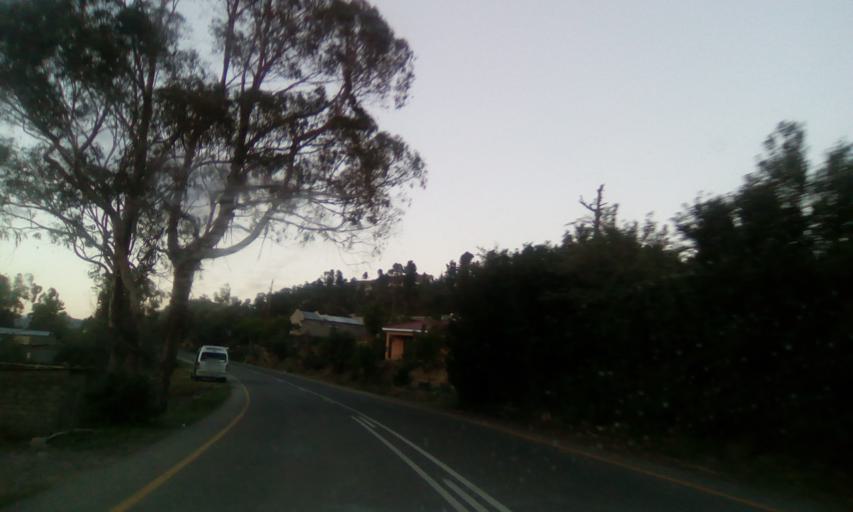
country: LS
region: Qacha's Nek
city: Qacha's Nek
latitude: -30.1273
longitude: 28.6889
